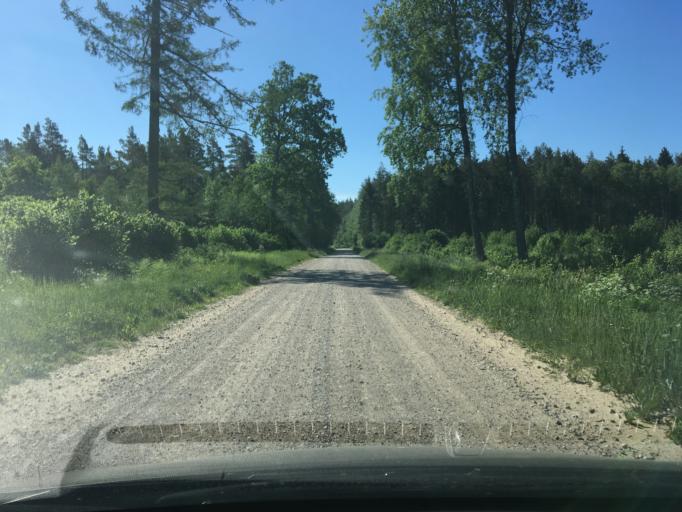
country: EE
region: Laeaene
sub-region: Lihula vald
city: Lihula
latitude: 58.6411
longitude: 23.7897
